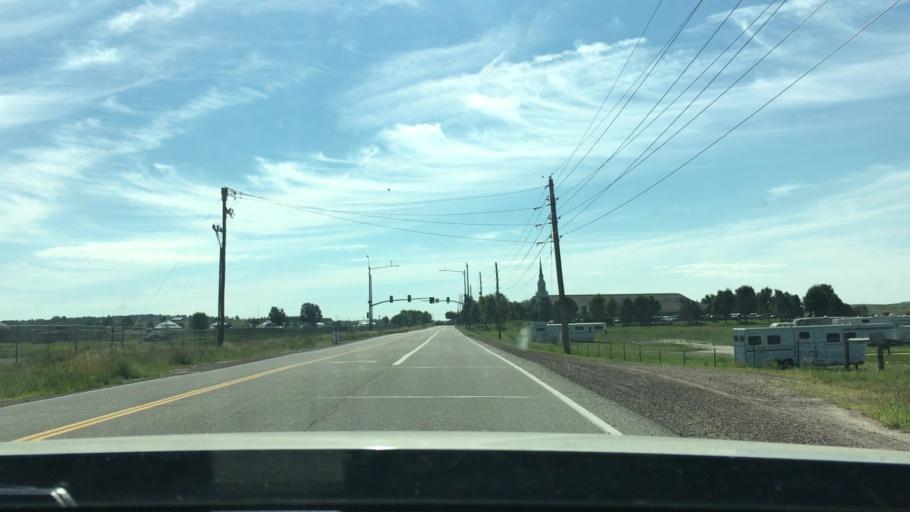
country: US
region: Colorado
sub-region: Douglas County
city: The Pinery
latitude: 39.4334
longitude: -104.7549
